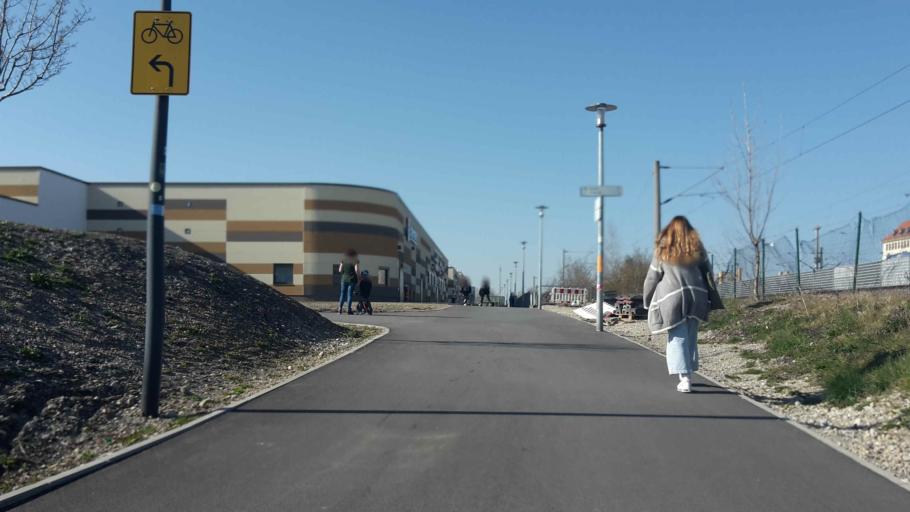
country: DE
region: Bavaria
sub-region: Upper Bavaria
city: Karlsfeld
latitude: 48.1872
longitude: 11.4689
